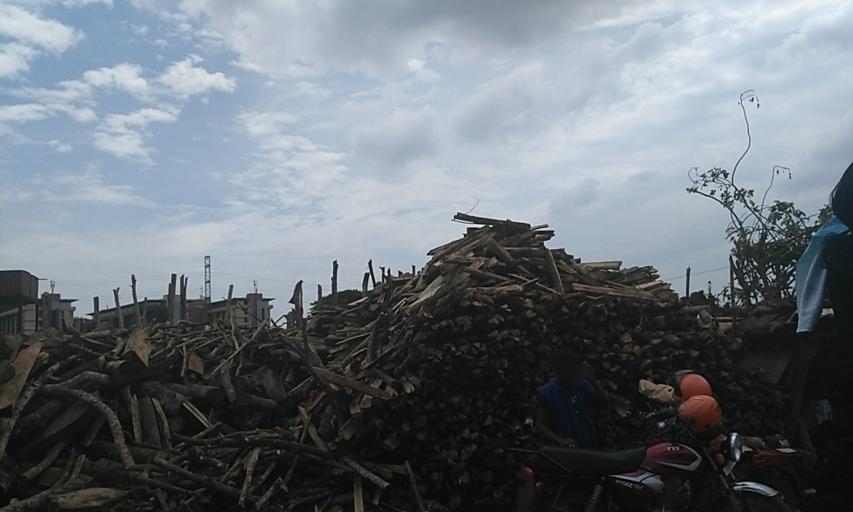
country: UG
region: Central Region
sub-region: Kampala District
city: Kampala
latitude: 0.3301
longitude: 32.6108
